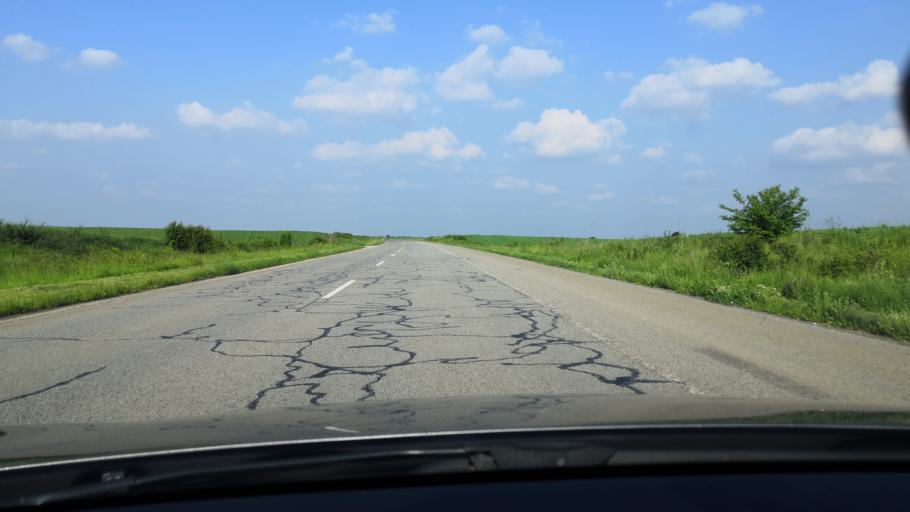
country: RS
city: Beska
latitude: 45.0906
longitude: 20.0553
